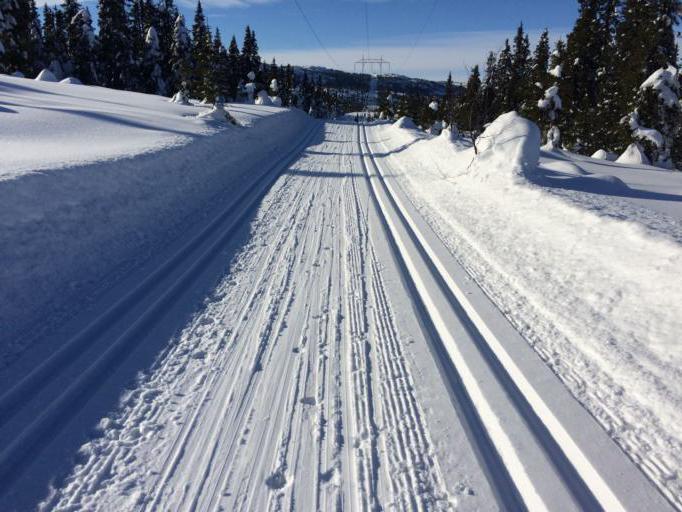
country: NO
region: Oppland
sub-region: Gausdal
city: Segalstad bru
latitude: 61.3191
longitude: 10.0909
